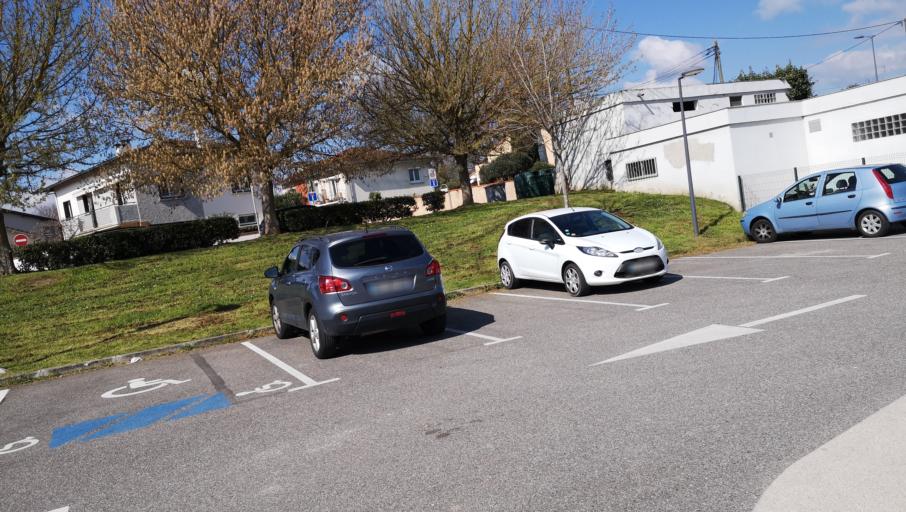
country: FR
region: Midi-Pyrenees
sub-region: Departement de la Haute-Garonne
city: Blagnac
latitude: 43.6389
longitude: 1.4004
